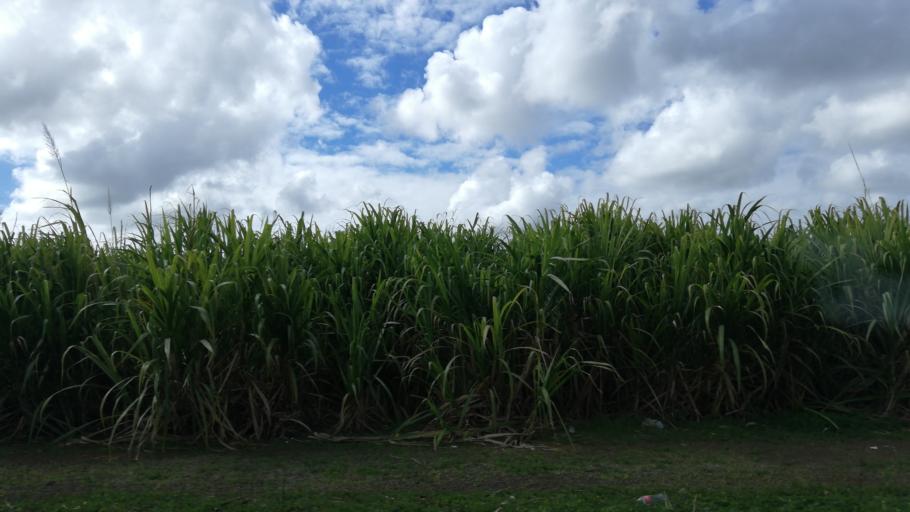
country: MU
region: Flacq
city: Camp de Masque
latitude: -20.2156
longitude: 57.6753
